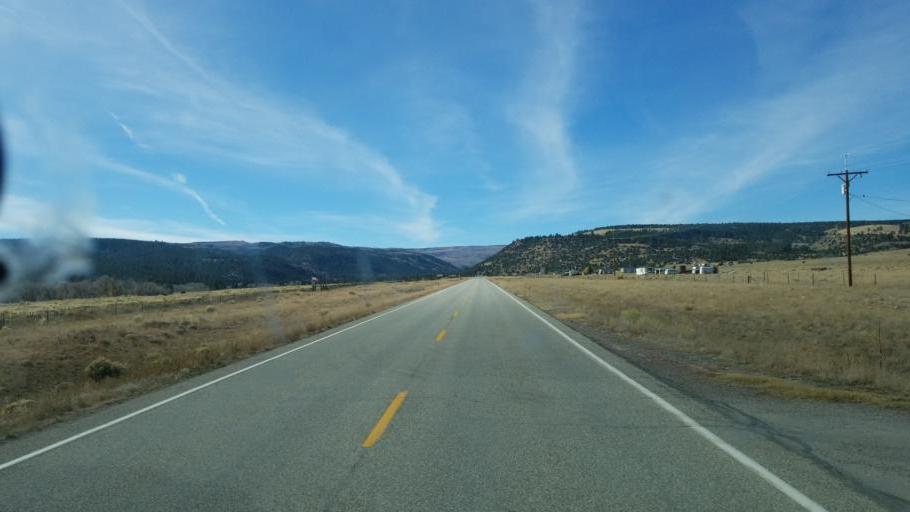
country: US
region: Colorado
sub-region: Conejos County
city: Conejos
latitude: 37.0670
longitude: -106.2042
